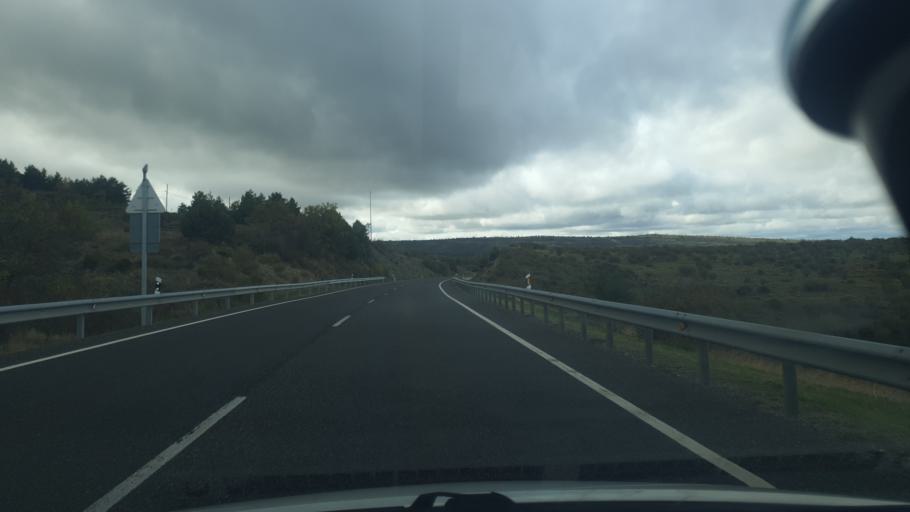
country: ES
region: Castille and Leon
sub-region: Provincia de Segovia
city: Torre Val de San Pedro
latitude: 41.0597
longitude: -3.8720
